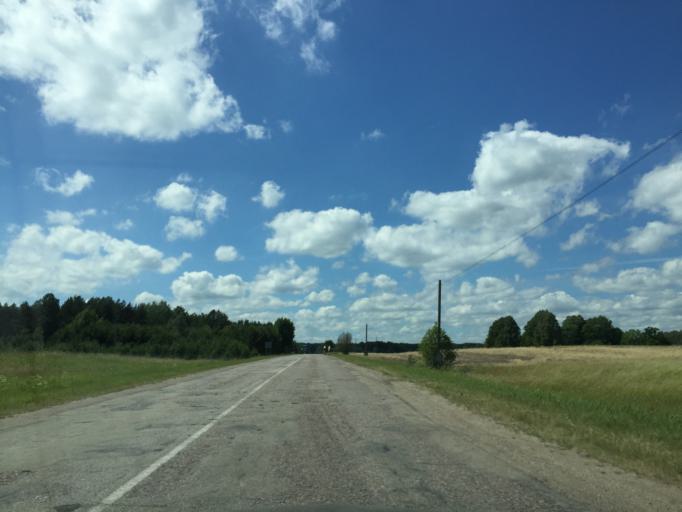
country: LV
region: Engure
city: Smarde
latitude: 56.9777
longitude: 23.3079
